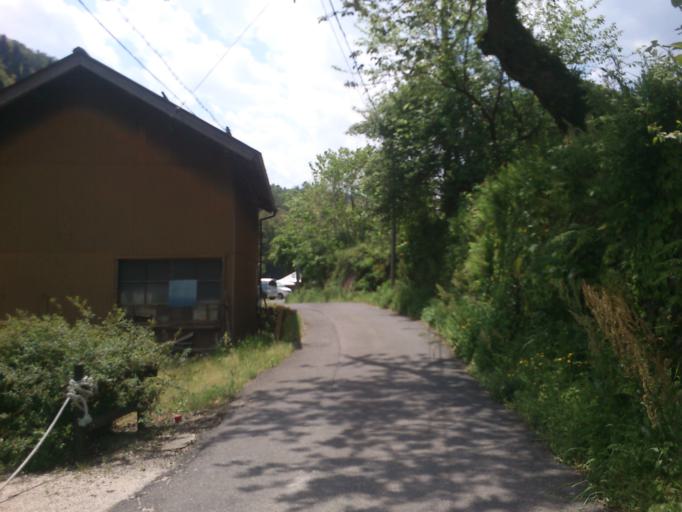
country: JP
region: Kyoto
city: Miyazu
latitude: 35.6816
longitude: 135.1697
